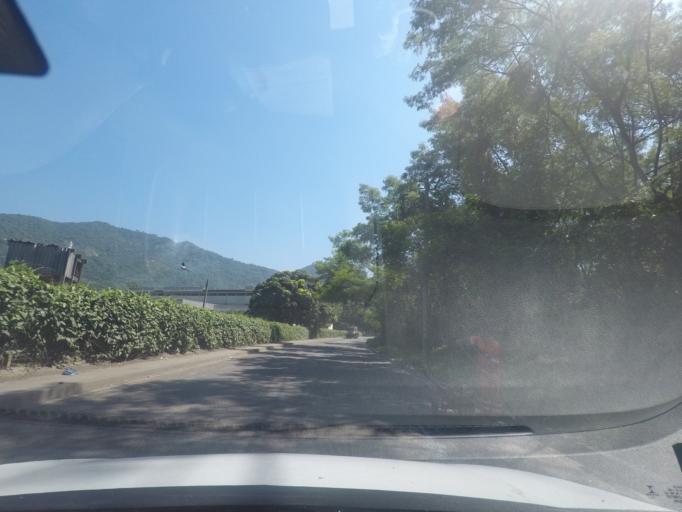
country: BR
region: Rio de Janeiro
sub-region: Nilopolis
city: Nilopolis
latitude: -22.9863
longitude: -43.4528
